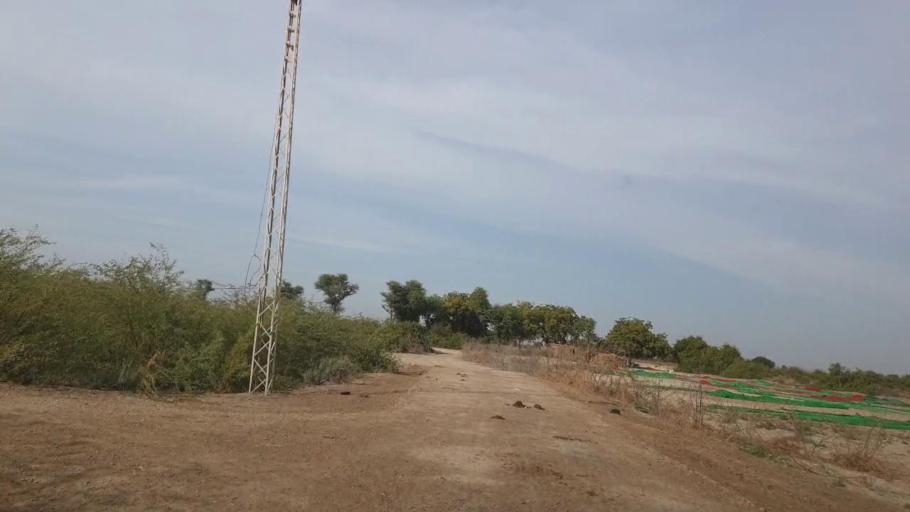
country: PK
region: Sindh
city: Nabisar
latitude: 24.9946
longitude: 69.5725
